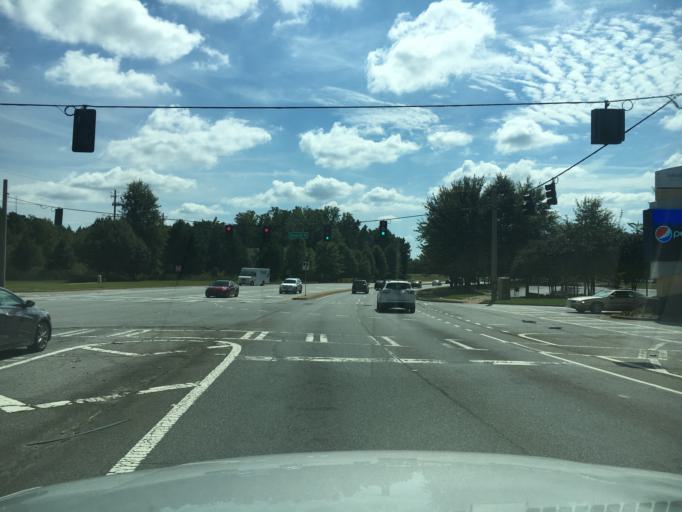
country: US
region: Georgia
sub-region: Gwinnett County
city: Duluth
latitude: 33.9963
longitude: -84.0920
